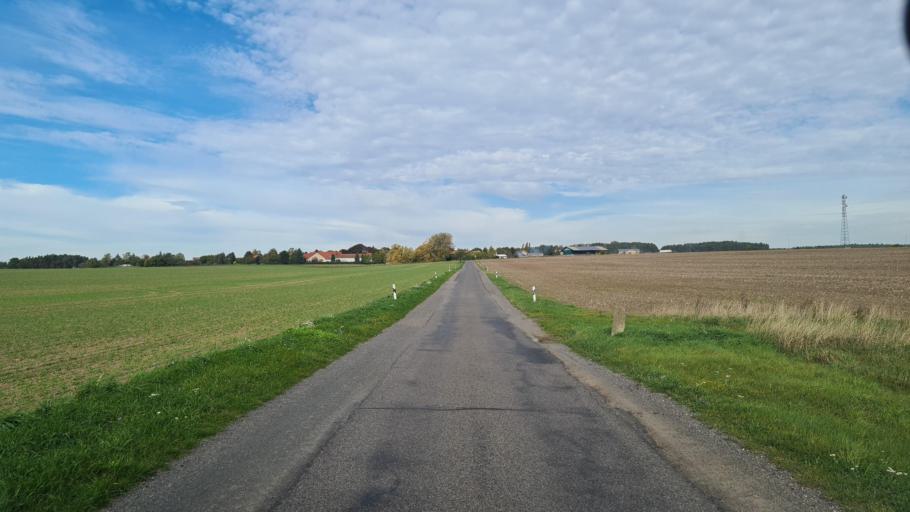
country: DE
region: Brandenburg
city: Linthe
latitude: 52.1053
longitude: 12.7540
